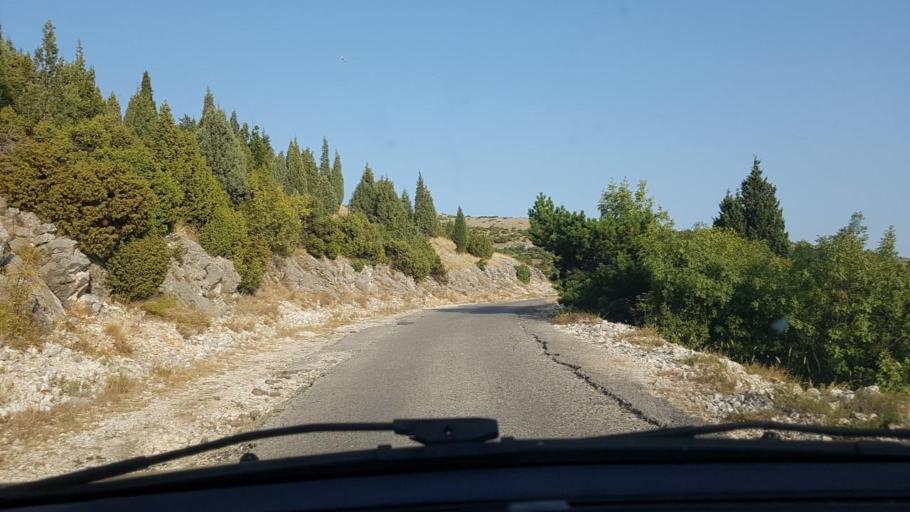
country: BA
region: Federation of Bosnia and Herzegovina
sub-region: Hercegovacko-Bosanski Kanton
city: Mostar
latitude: 43.3486
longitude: 17.8283
